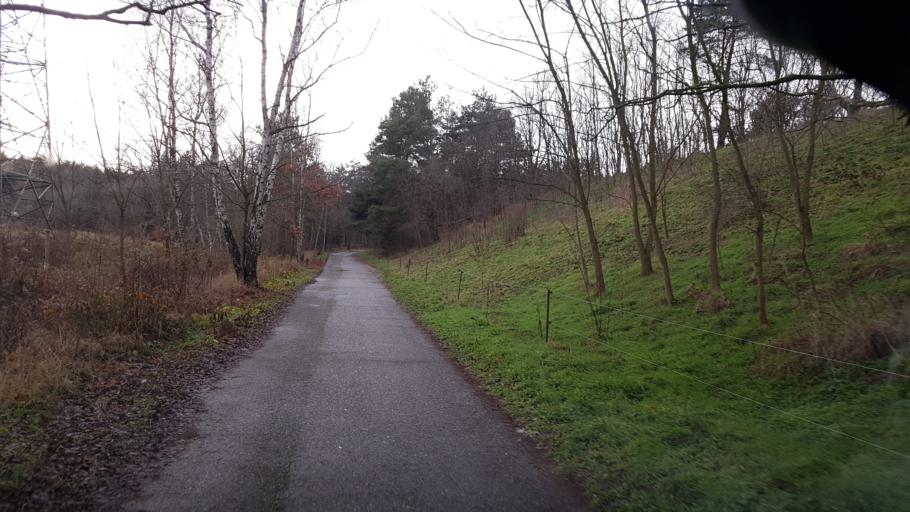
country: DE
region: Brandenburg
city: Altdobern
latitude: 51.6520
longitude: 14.0121
